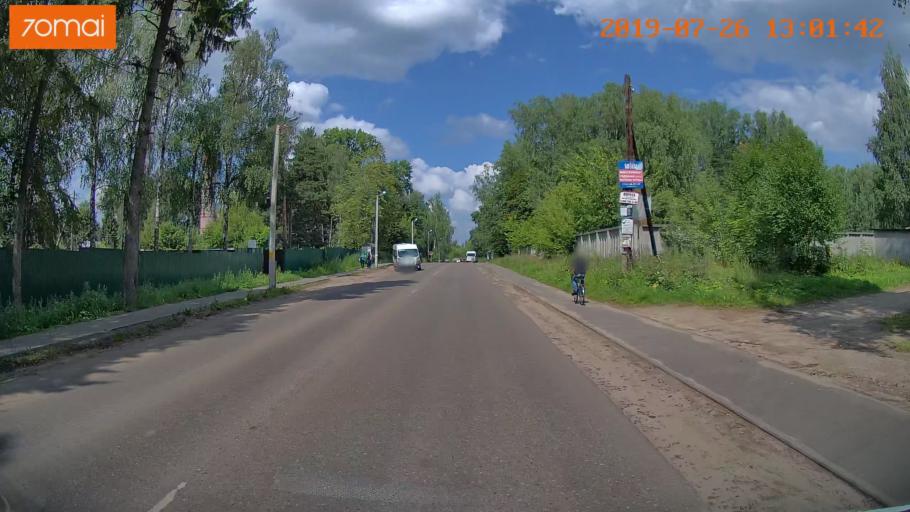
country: RU
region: Ivanovo
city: Bogorodskoye
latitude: 57.0398
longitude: 41.0124
